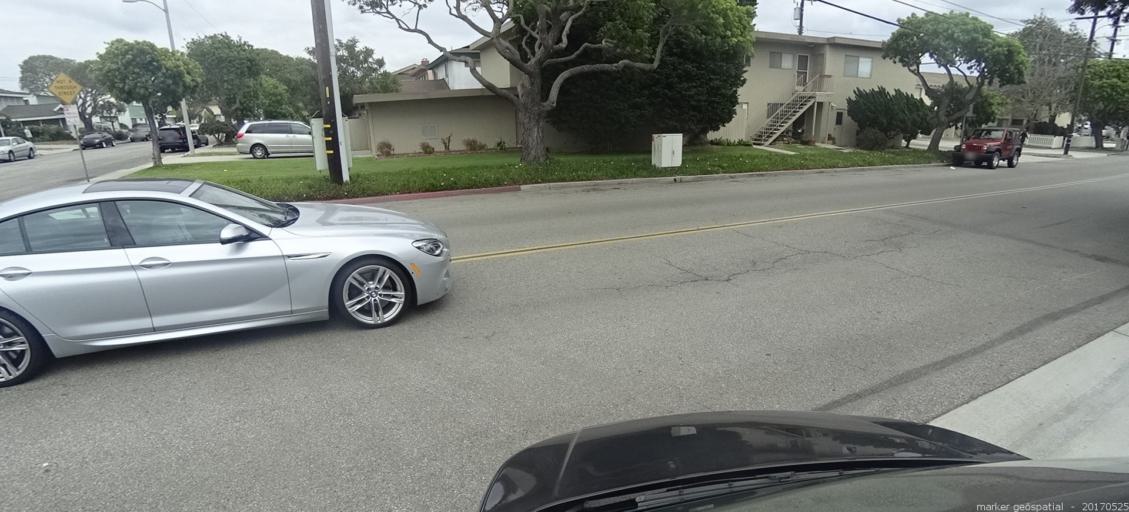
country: US
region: California
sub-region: Los Angeles County
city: Redondo Beach
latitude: 33.8555
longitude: -118.3806
